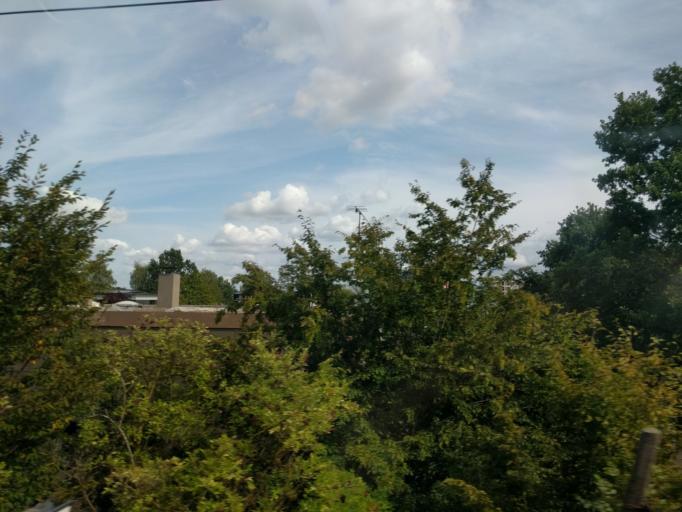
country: DE
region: Schleswig-Holstein
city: Ahrensburg
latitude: 53.6778
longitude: 10.2473
